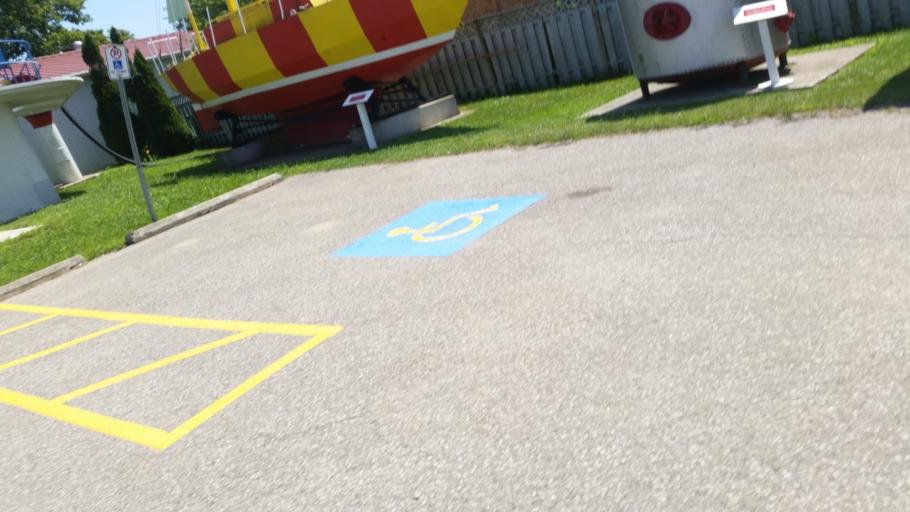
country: CA
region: Ontario
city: Aylmer
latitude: 42.6455
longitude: -80.8062
